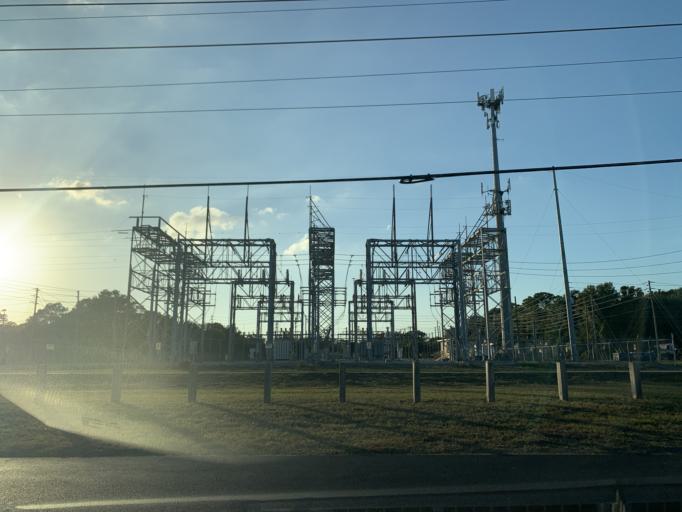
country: US
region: Florida
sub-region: Pinellas County
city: South Highpoint
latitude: 27.9555
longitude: -82.7333
